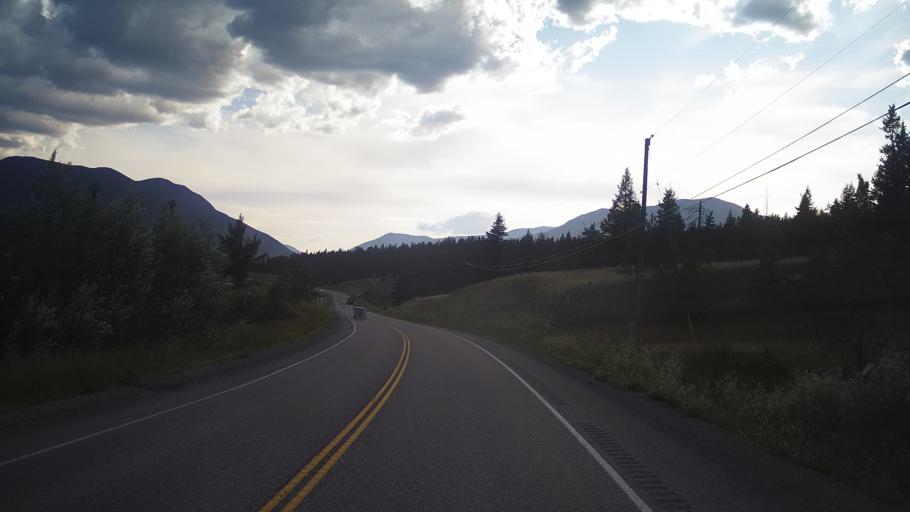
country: CA
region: British Columbia
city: Cache Creek
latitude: 51.1056
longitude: -121.5540
